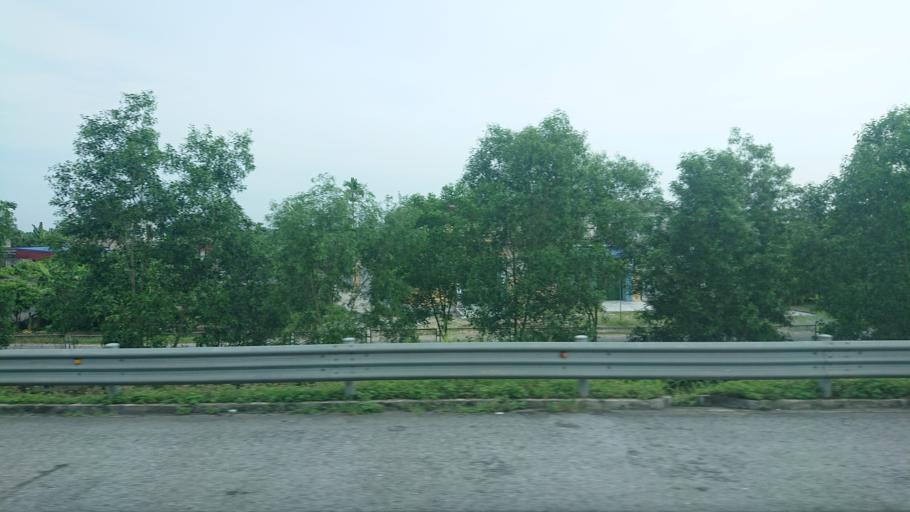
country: VN
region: Hai Duong
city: Tu Ky
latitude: 20.8240
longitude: 106.4674
